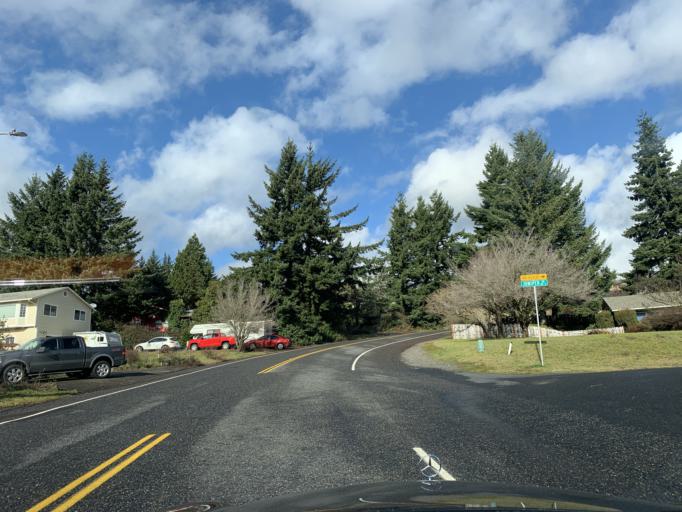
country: US
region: Washington
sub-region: Skamania County
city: Carson
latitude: 45.7199
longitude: -121.8174
